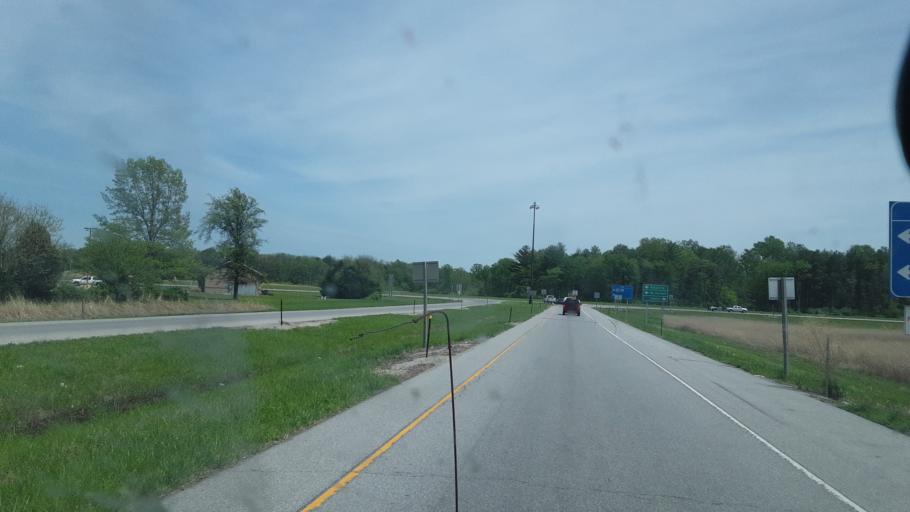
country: US
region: Illinois
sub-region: Edwards County
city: Grayville
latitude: 38.2362
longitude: -88.0033
